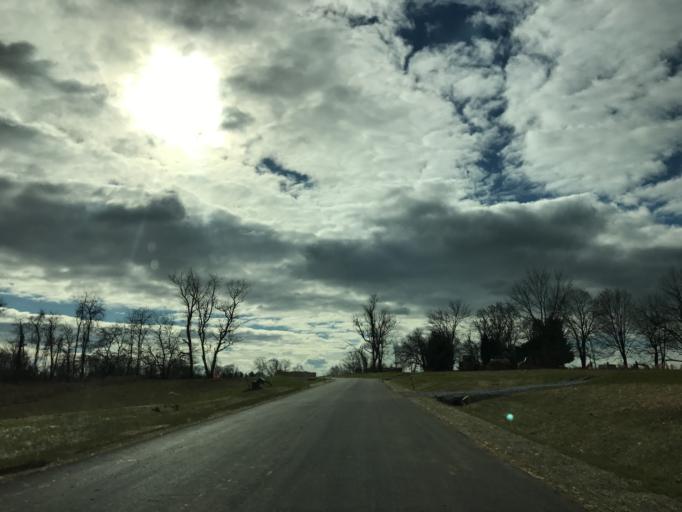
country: US
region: Maryland
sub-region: Harford County
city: Jarrettsville
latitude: 39.5150
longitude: -76.5293
